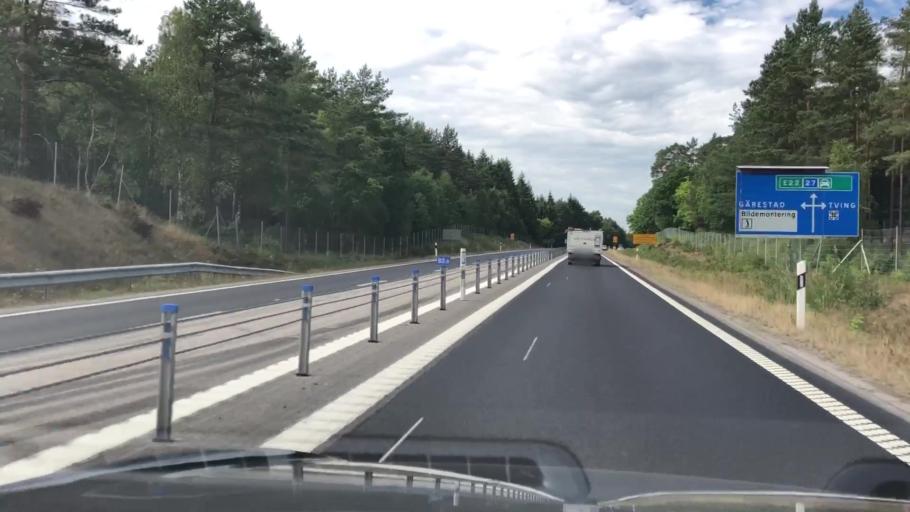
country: SE
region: Blekinge
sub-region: Ronneby Kommun
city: Kallinge
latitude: 56.1996
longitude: 15.3840
